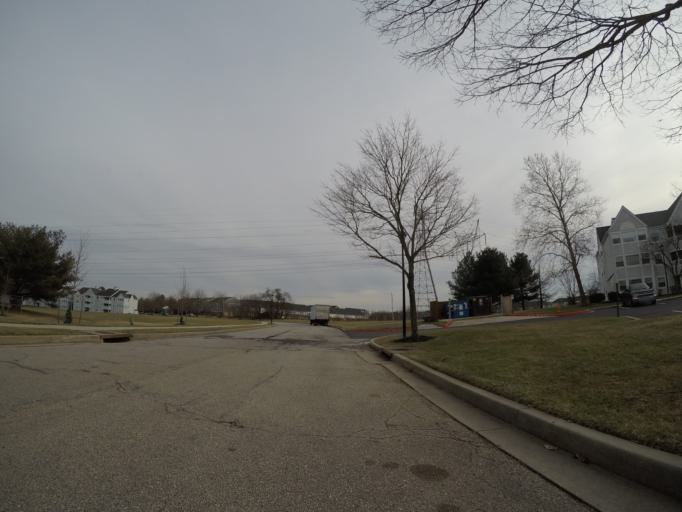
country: US
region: Maryland
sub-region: Howard County
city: Columbia
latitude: 39.2181
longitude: -76.8006
